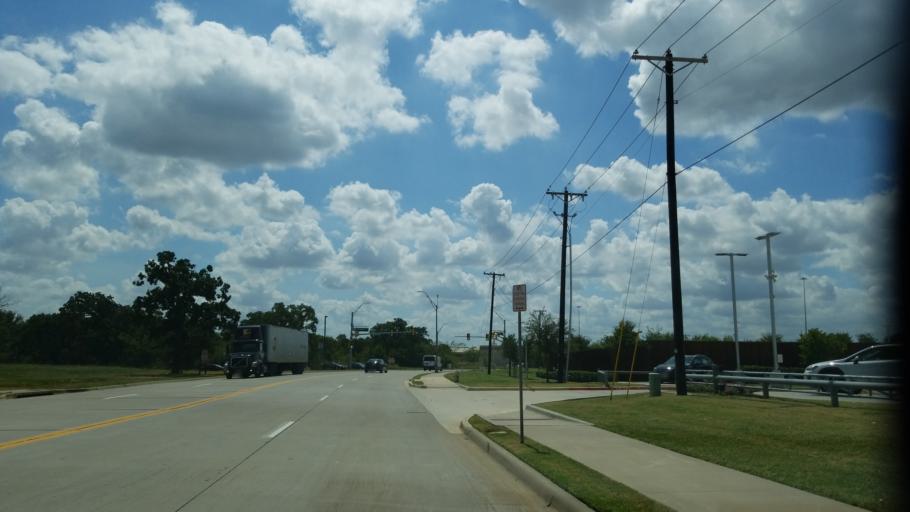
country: US
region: Texas
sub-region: Tarrant County
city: Grapevine
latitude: 32.9065
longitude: -97.0944
